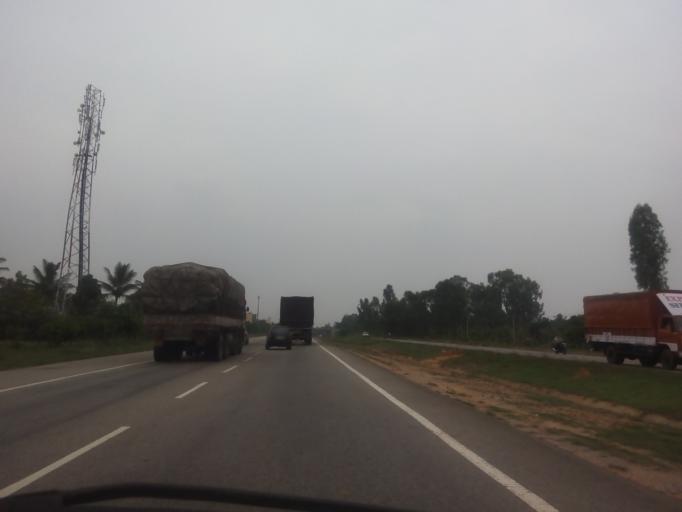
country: IN
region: Karnataka
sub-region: Bangalore Urban
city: Bangalore
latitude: 12.8643
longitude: 77.6447
